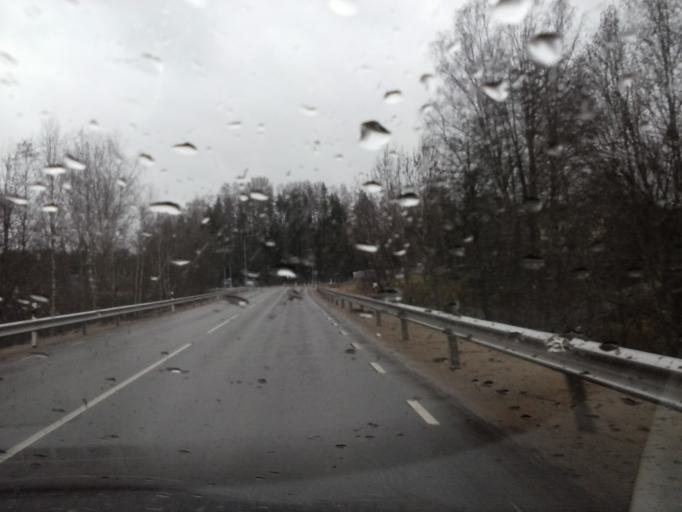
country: EE
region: Polvamaa
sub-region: Polva linn
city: Polva
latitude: 58.0443
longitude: 27.0725
